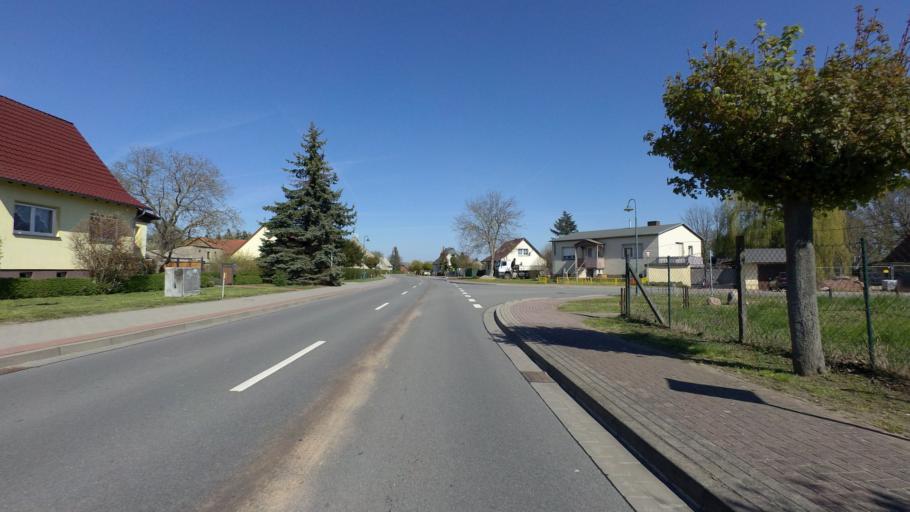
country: DE
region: Saxony-Anhalt
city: Kalbe
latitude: 52.6473
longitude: 11.3392
